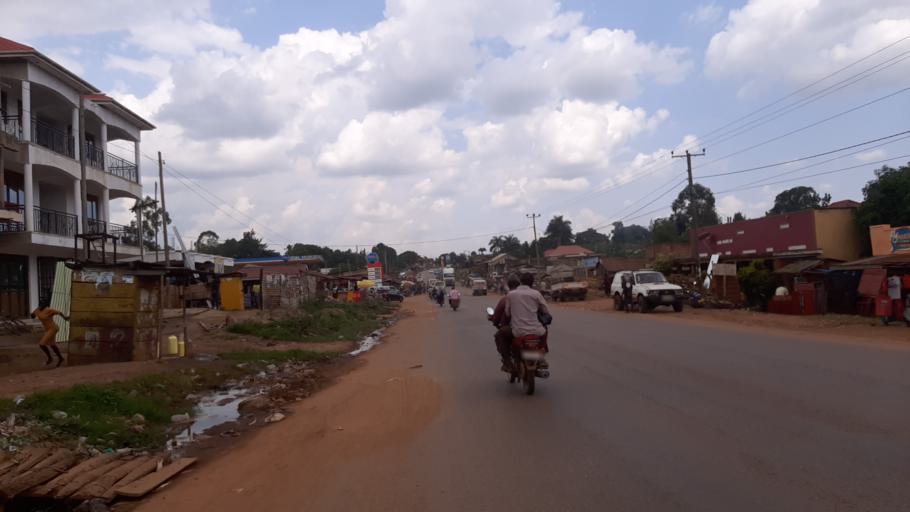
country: UG
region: Eastern Region
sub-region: Mbale District
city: Mbale
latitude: 1.0469
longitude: 34.1779
